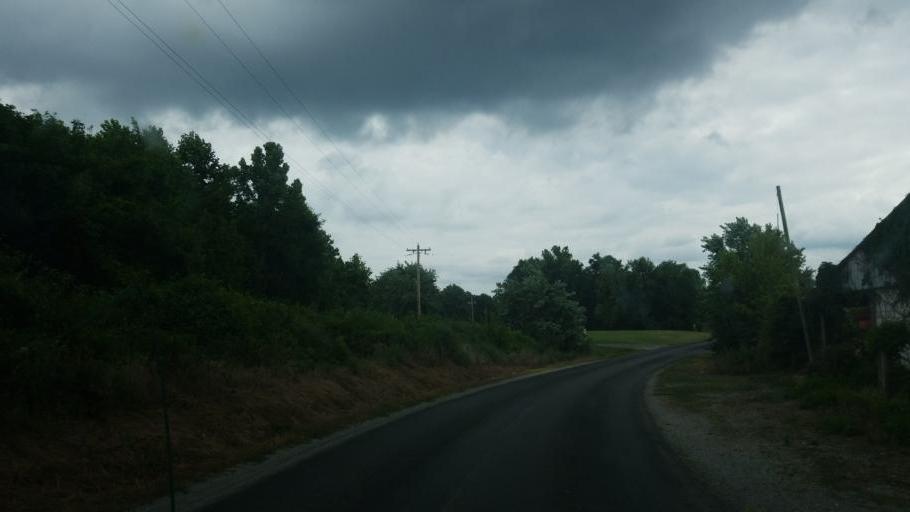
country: US
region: Illinois
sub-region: Jackson County
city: Murphysboro
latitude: 37.7062
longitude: -89.3316
